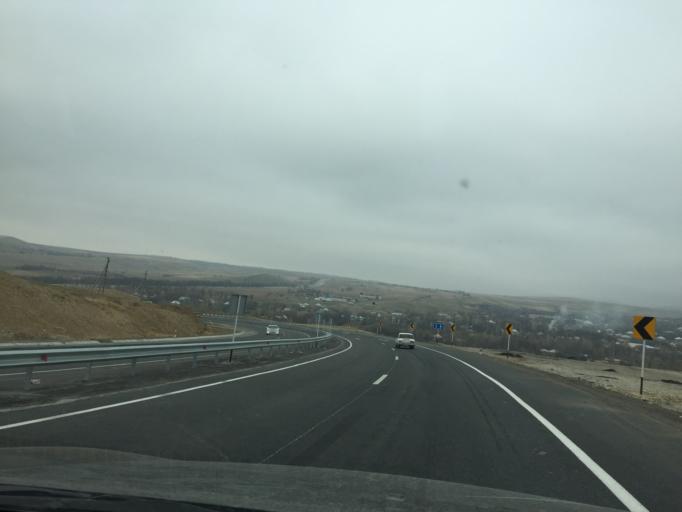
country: KZ
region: Ongtustik Qazaqstan
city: Sastobe
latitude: 42.4927
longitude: 69.9581
